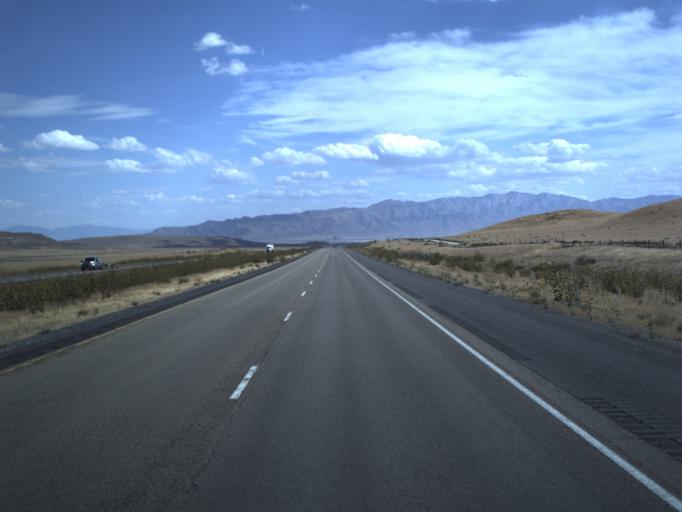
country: US
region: Utah
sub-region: Tooele County
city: Grantsville
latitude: 40.8132
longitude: -112.8739
